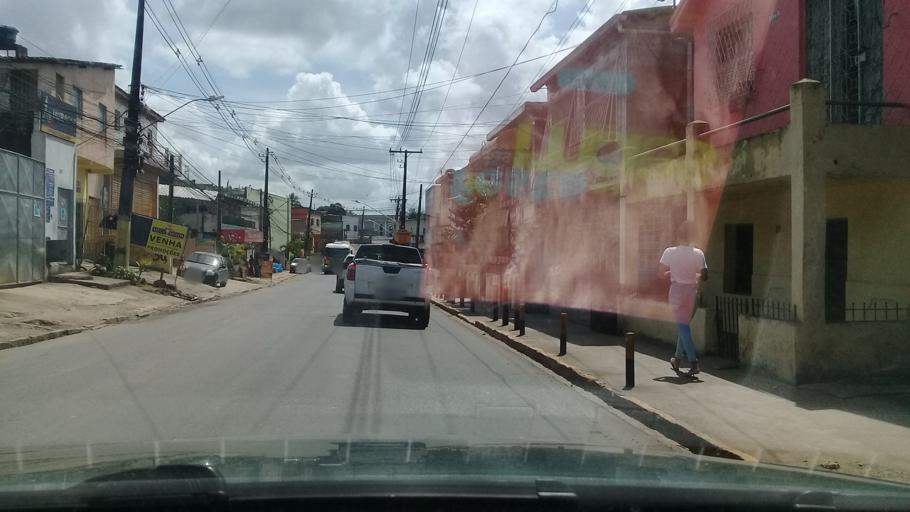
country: BR
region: Pernambuco
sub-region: Jaboatao Dos Guararapes
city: Jaboatao dos Guararapes
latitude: -8.0996
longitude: -35.0203
